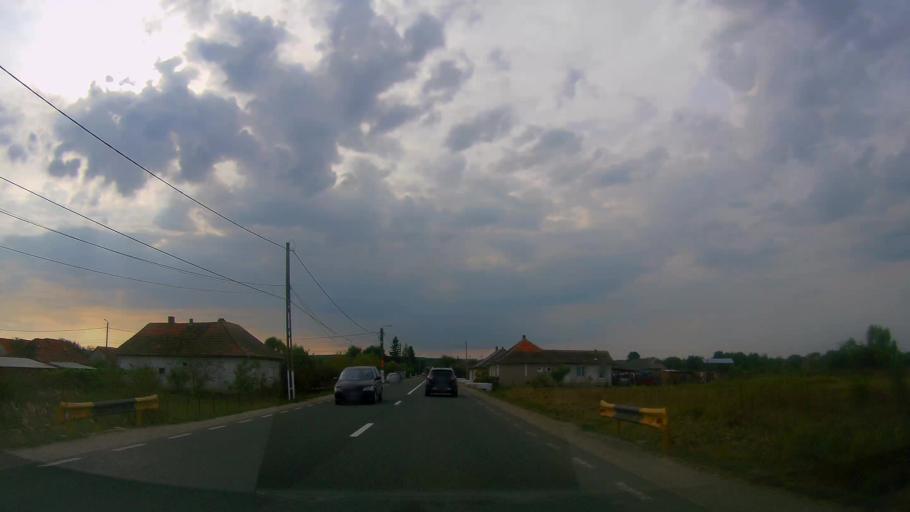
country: RO
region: Satu Mare
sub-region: Oras Ardud
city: Ardud
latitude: 47.5888
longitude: 22.8831
